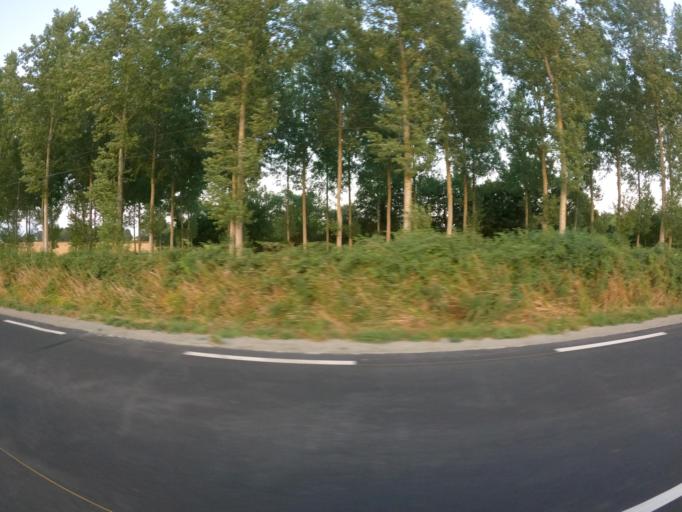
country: FR
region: Pays de la Loire
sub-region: Departement de la Mayenne
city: Chemaze
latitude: 47.7578
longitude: -0.7887
